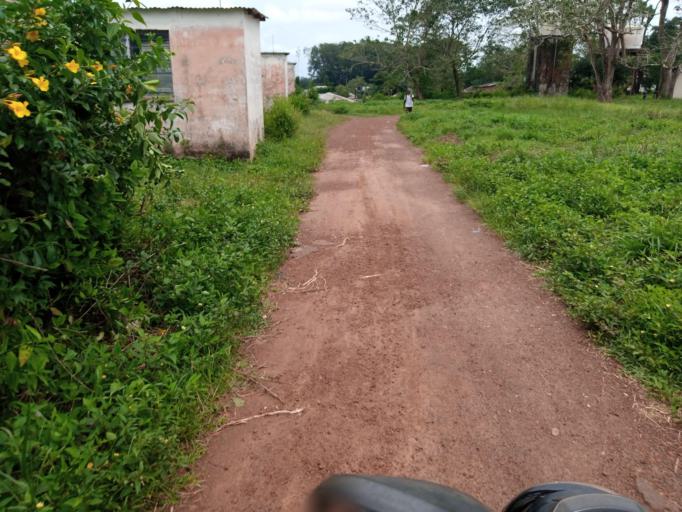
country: SL
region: Southern Province
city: Largo
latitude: 8.1988
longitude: -12.0642
